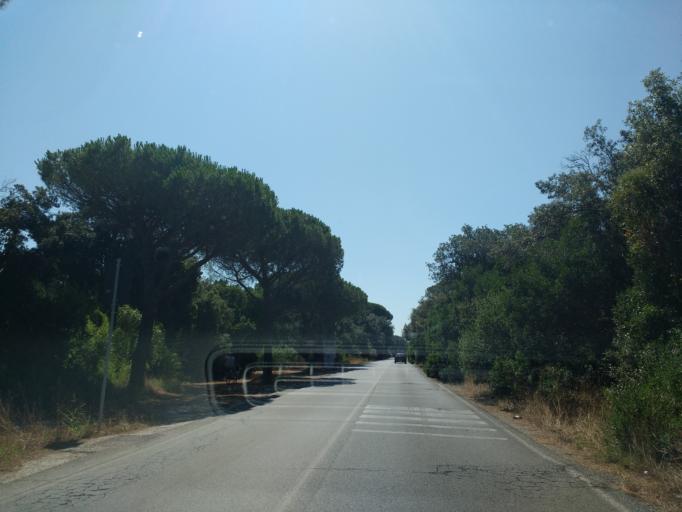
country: IT
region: Latium
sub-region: Citta metropolitana di Roma Capitale
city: Acilia-Castel Fusano-Ostia Antica
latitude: 41.7158
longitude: 12.3535
